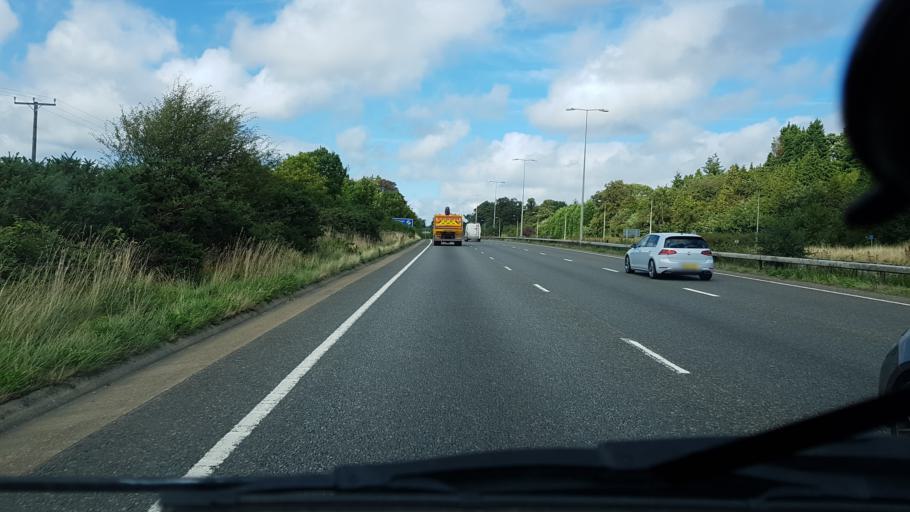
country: GB
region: England
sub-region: West Sussex
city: Broadfield
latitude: 51.0702
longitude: -0.2048
